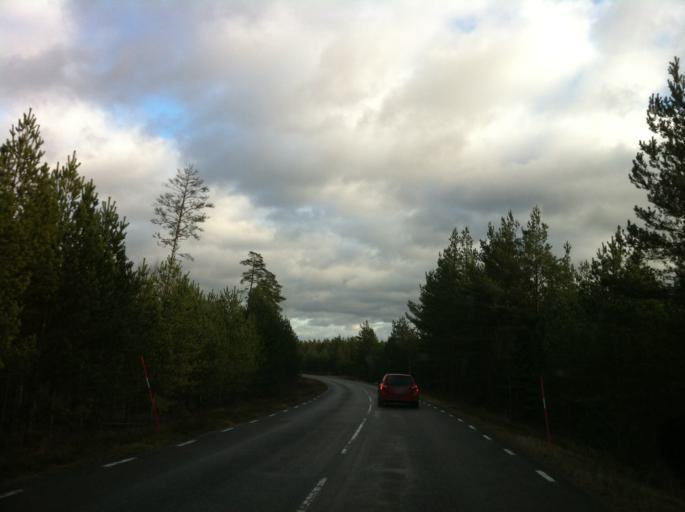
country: SE
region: Kalmar
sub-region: Hultsfreds Kommun
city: Hultsfred
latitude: 57.5242
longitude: 15.7191
